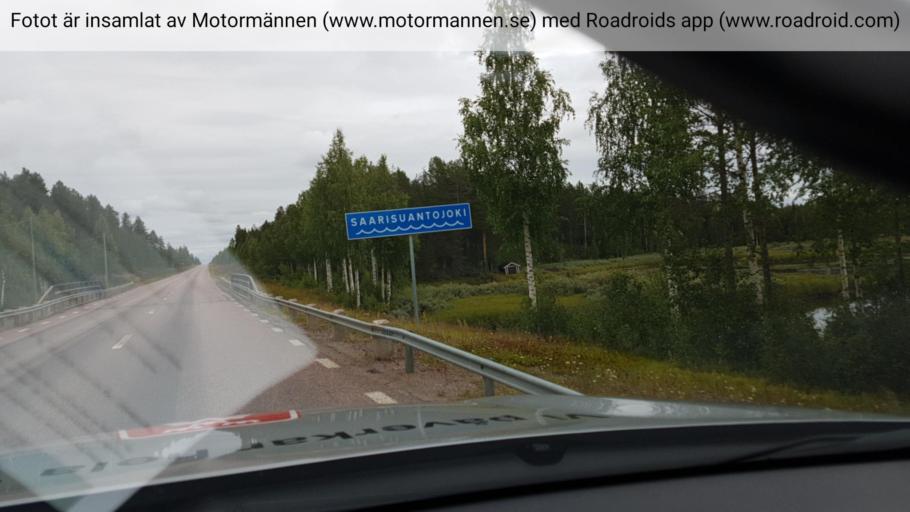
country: SE
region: Norrbotten
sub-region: Overkalix Kommun
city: OEverkalix
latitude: 67.0796
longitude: 22.5379
